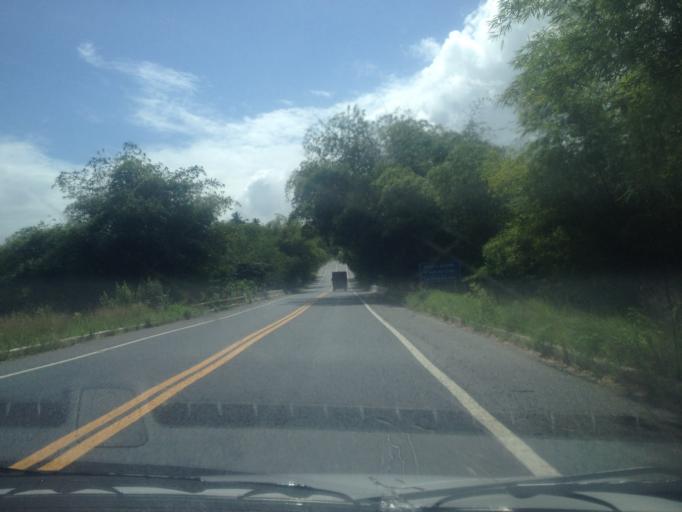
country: BR
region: Sergipe
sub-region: Indiaroba
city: Indiaroba
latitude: -11.6148
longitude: -37.5374
